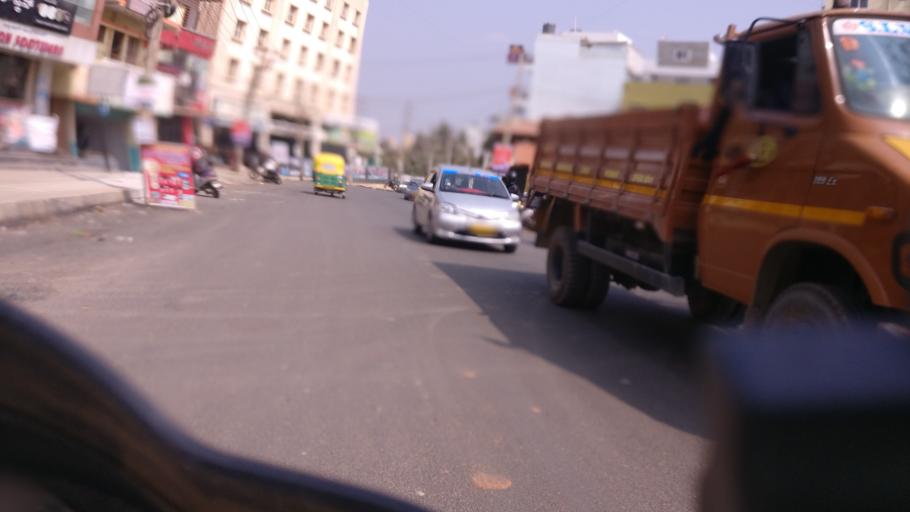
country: IN
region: Karnataka
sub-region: Bangalore Urban
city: Bangalore
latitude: 12.9053
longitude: 77.6759
